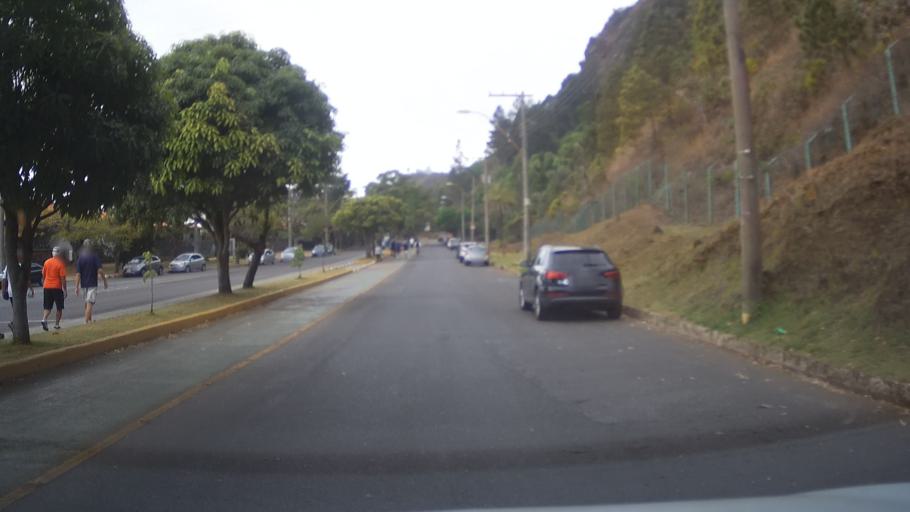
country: BR
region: Minas Gerais
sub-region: Belo Horizonte
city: Belo Horizonte
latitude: -19.9566
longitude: -43.9097
